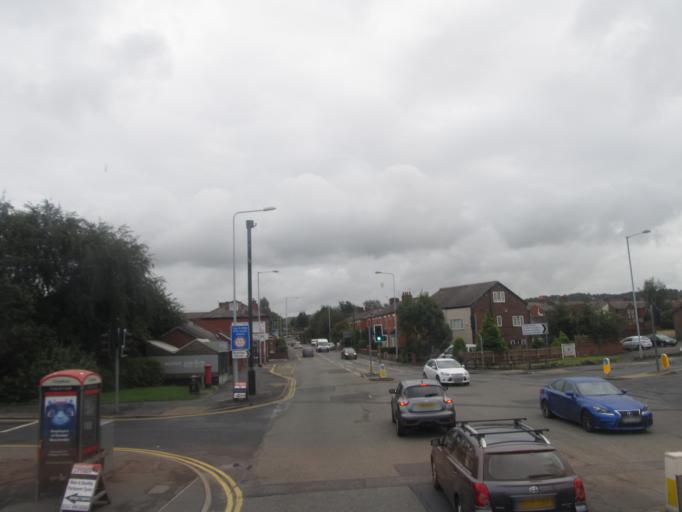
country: GB
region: England
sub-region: Borough of Stockport
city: Bredbury
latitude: 53.4226
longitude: -2.1149
